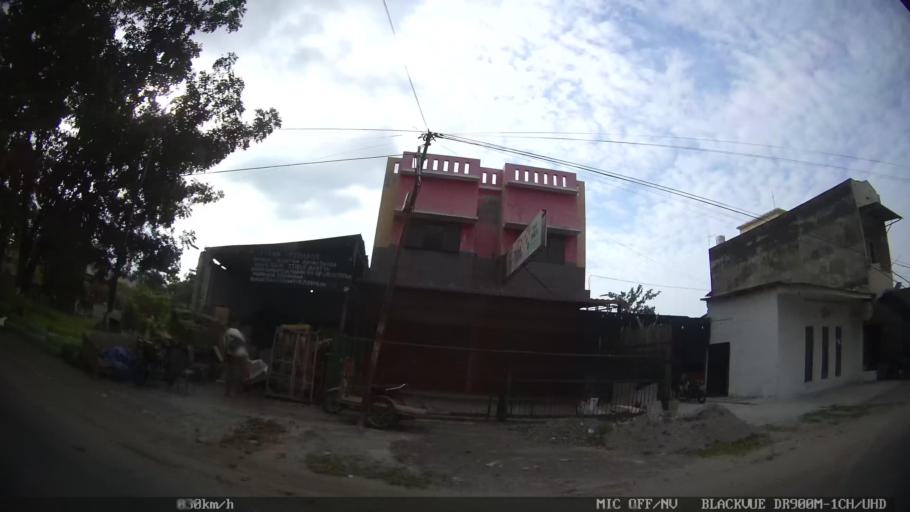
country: ID
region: North Sumatra
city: Sunggal
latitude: 3.5569
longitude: 98.6160
